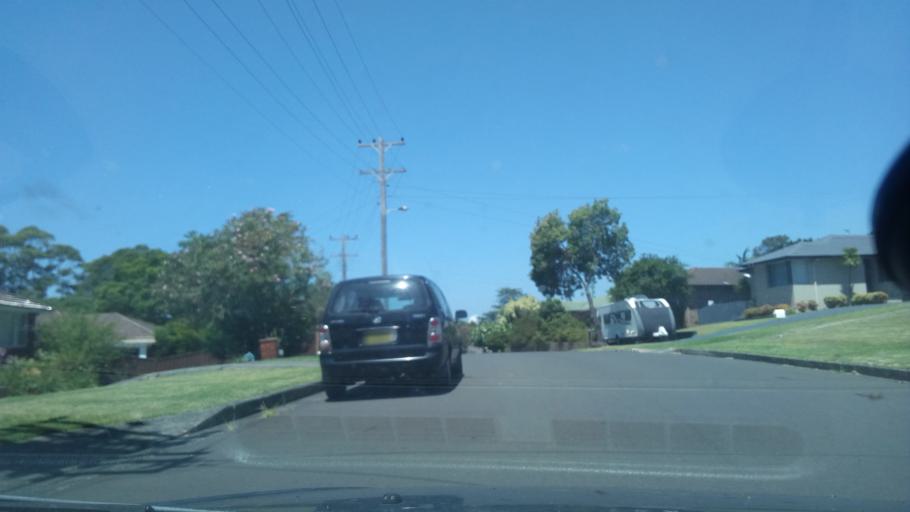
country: AU
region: New South Wales
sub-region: Wollongong
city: West Wollongong
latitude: -34.4243
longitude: 150.8589
